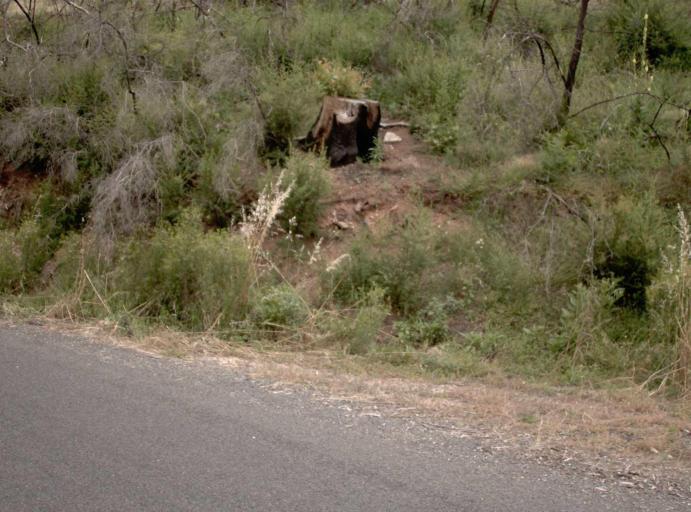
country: AU
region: Victoria
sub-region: Wellington
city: Heyfield
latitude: -37.8594
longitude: 146.7073
